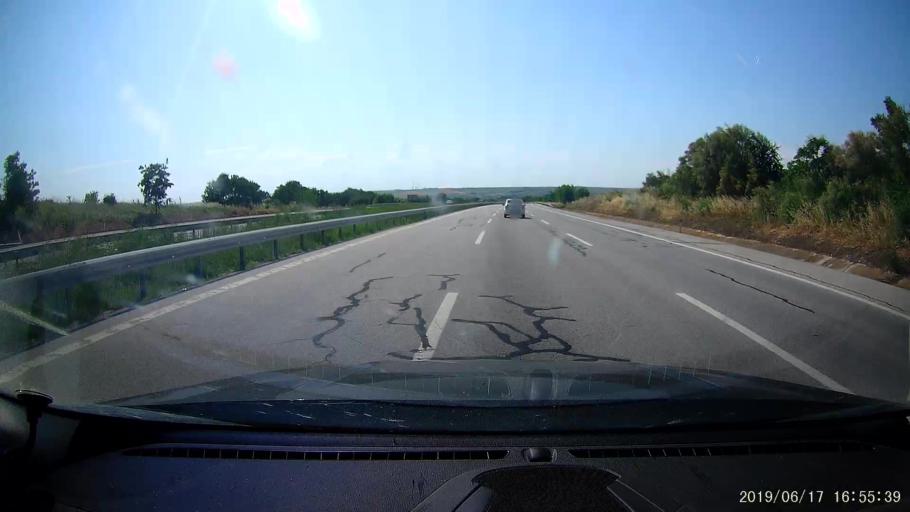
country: TR
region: Edirne
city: Haskoy
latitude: 41.5801
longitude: 26.9594
